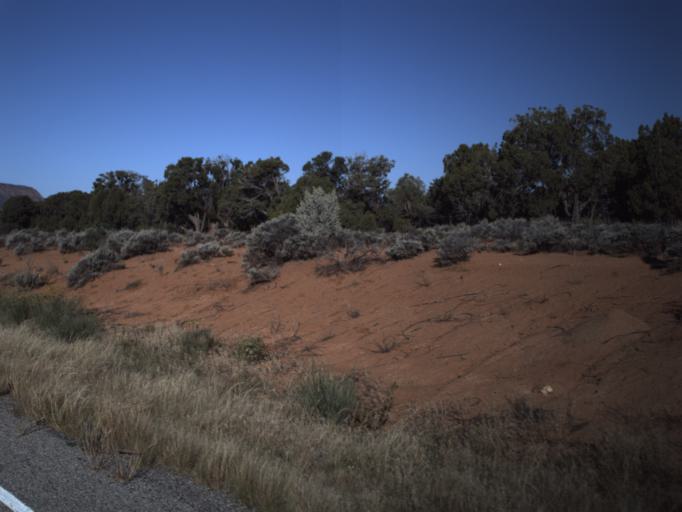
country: US
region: Utah
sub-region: San Juan County
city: Blanding
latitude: 37.5408
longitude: -109.9602
